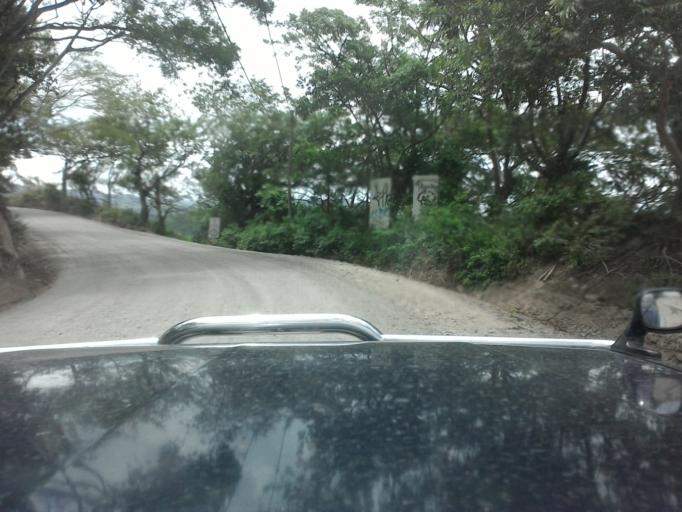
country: CR
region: Guanacaste
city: Juntas
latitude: 10.2234
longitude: -84.8509
